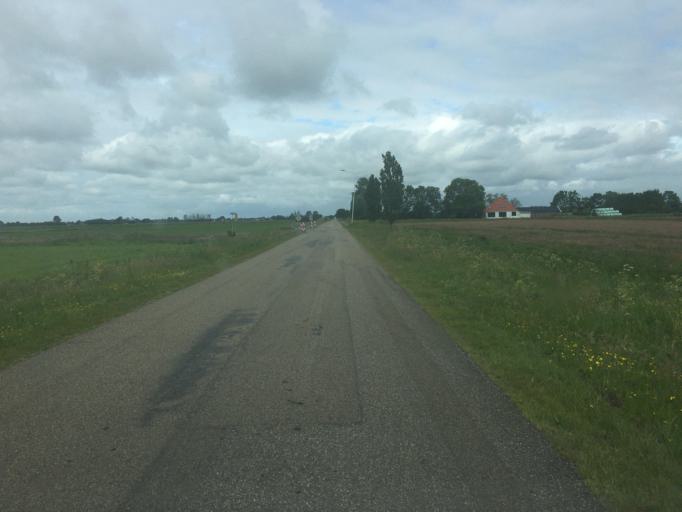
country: NL
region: Friesland
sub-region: Gemeente Skarsterlan
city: Oudehaske
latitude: 52.9081
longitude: 5.8729
